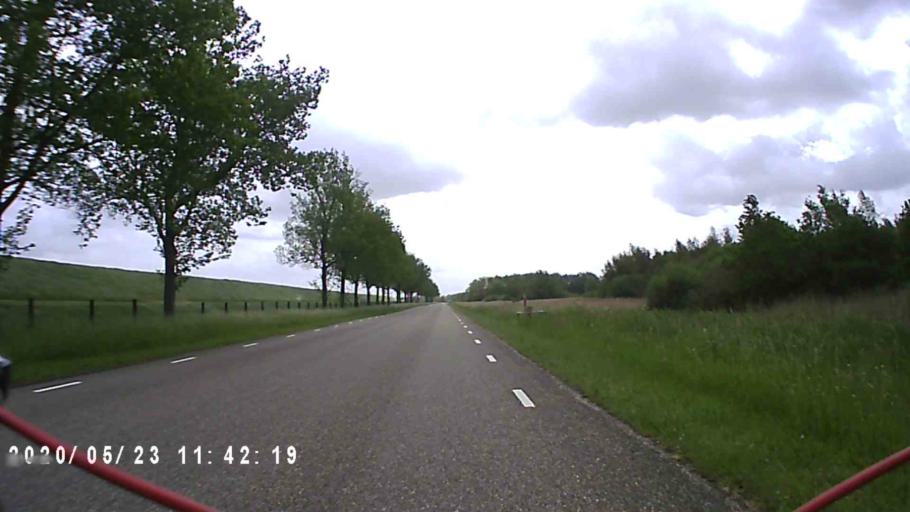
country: NL
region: Groningen
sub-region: Gemeente Delfzijl
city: Delfzijl
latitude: 53.3047
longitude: 7.0128
